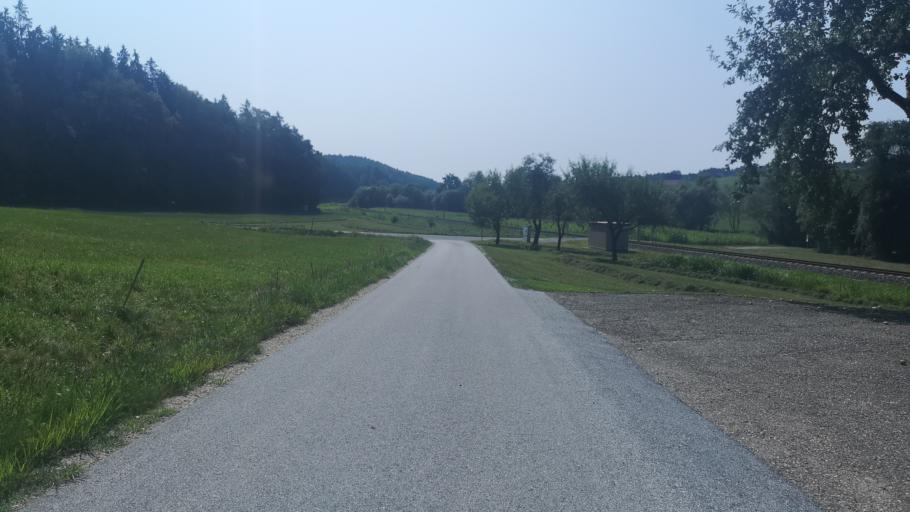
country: AT
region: Styria
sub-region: Politischer Bezirk Deutschlandsberg
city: Lannach
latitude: 46.9326
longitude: 15.3438
